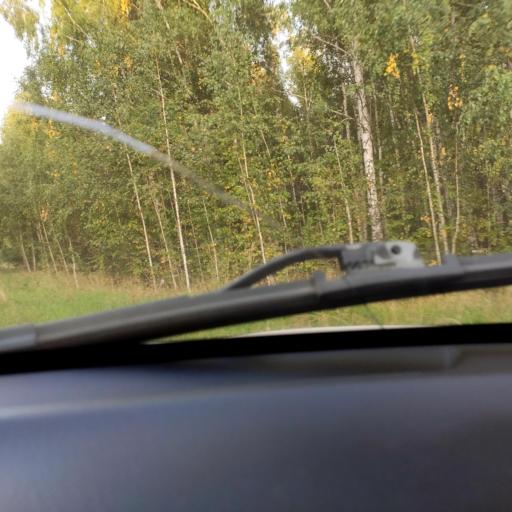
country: RU
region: Tatarstan
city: Verkhniy Uslon
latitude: 55.6595
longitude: 48.9576
